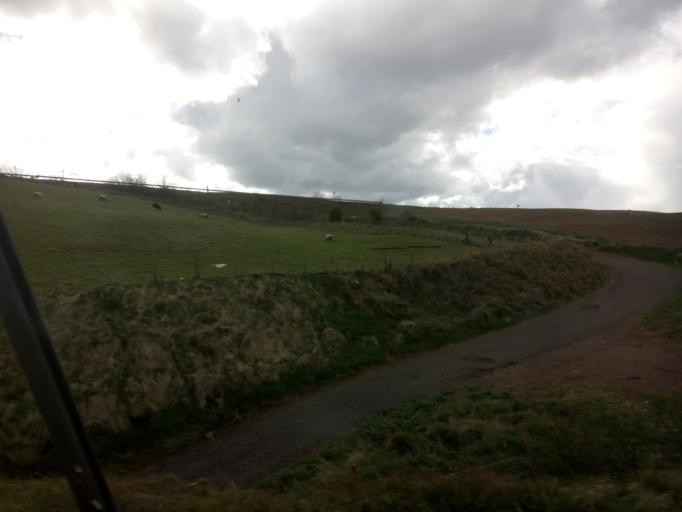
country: GB
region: Scotland
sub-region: The Scottish Borders
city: Eyemouth
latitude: 55.8391
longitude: -2.0686
